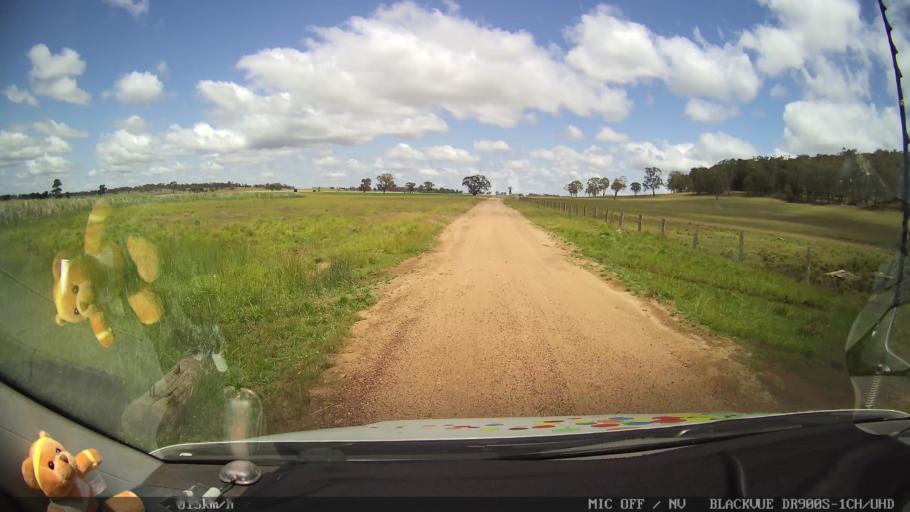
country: AU
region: New South Wales
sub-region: Glen Innes Severn
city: Glen Innes
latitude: -29.5947
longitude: 151.6656
